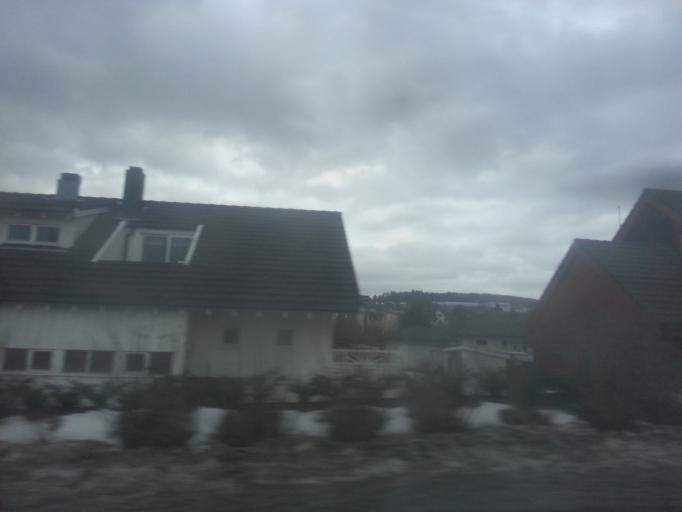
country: NO
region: Sor-Trondelag
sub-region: Trondheim
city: Trondheim
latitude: 63.4253
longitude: 10.4580
